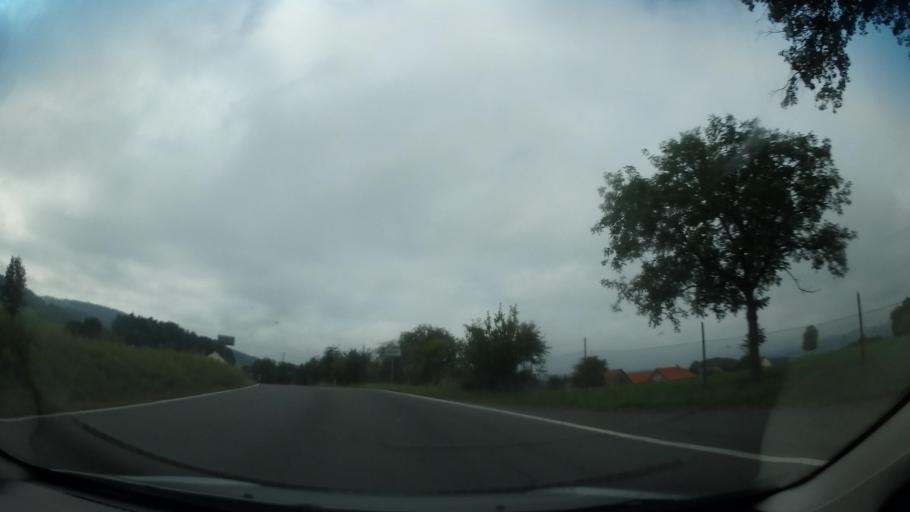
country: CZ
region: Central Bohemia
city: Kosova Hora
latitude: 49.7142
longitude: 14.4578
